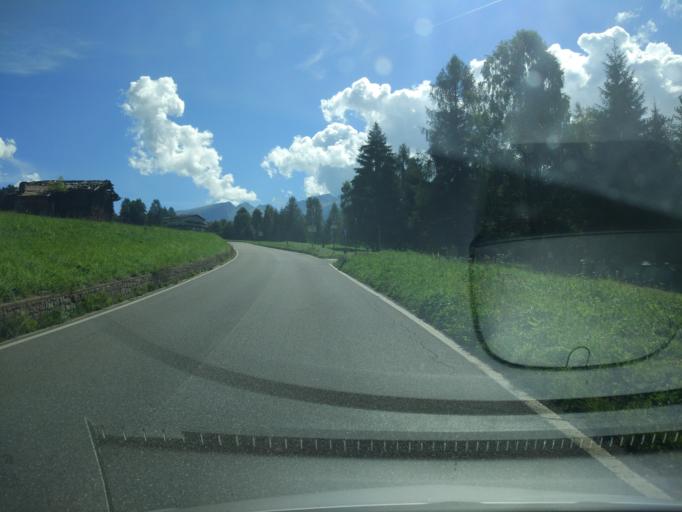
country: IT
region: Trentino-Alto Adige
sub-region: Provincia di Trento
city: Predazzo
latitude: 46.3161
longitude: 11.6550
